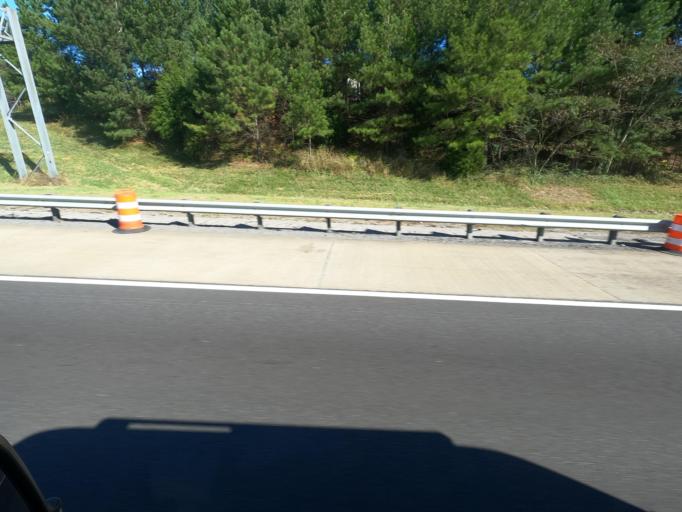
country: US
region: Tennessee
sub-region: Dickson County
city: Burns
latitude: 36.0207
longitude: -87.2605
